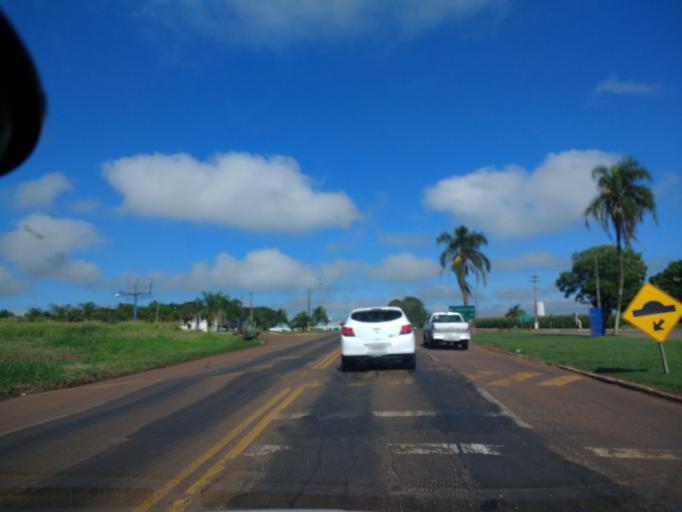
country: BR
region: Parana
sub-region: Paicandu
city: Paicandu
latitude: -23.5460
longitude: -52.2298
